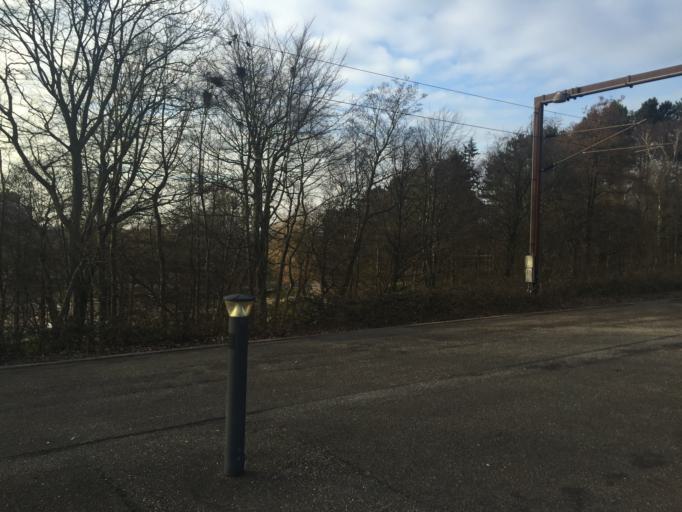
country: DK
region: South Denmark
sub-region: Fredericia Kommune
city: Fredericia
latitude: 55.5695
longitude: 9.7397
